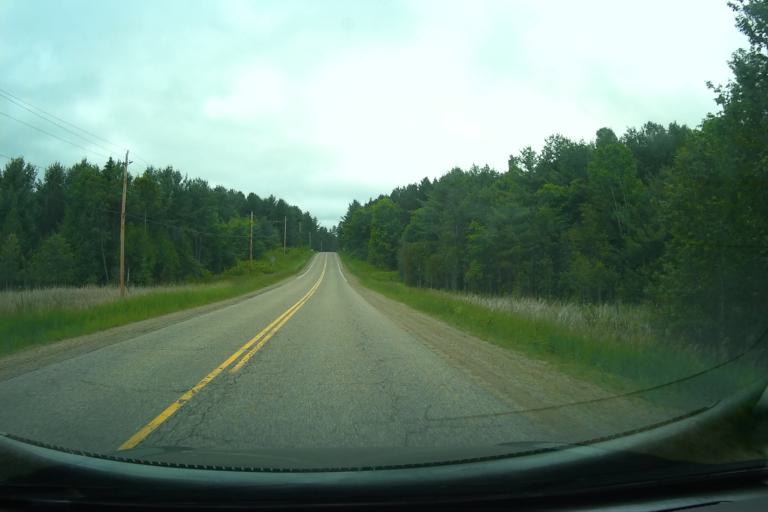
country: CA
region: Ontario
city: Pembroke
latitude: 45.4938
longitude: -77.1719
